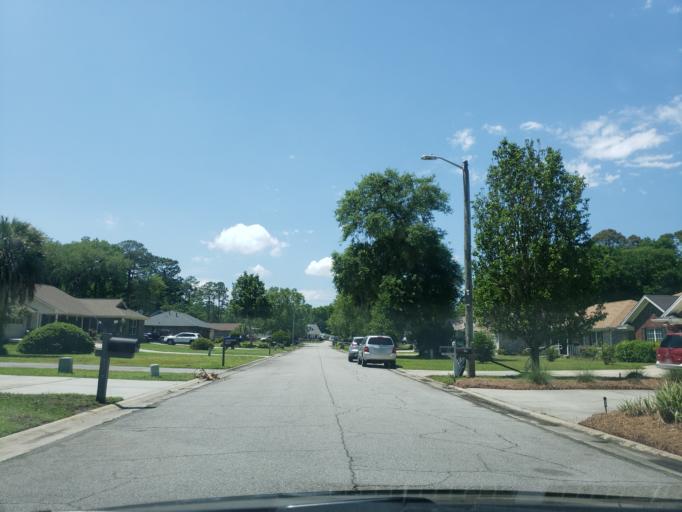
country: US
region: Georgia
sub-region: Chatham County
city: Isle of Hope
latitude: 31.9771
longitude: -81.0824
